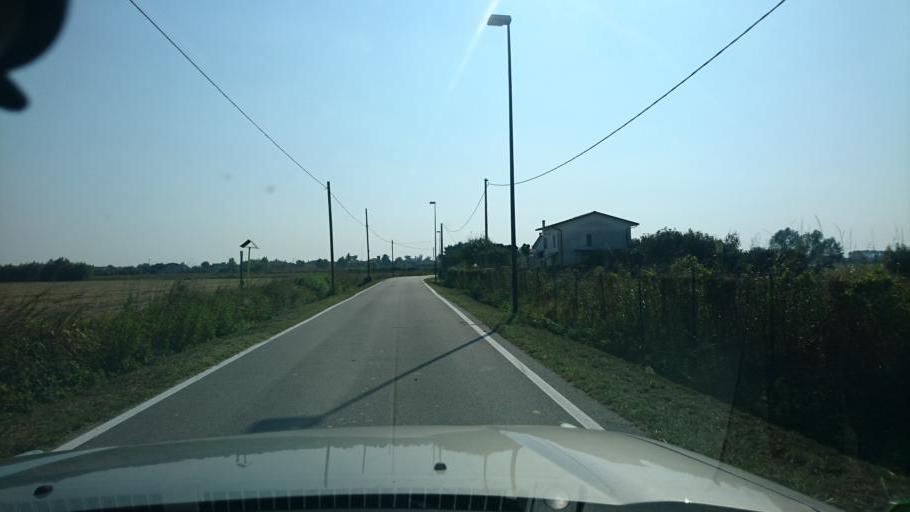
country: IT
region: Veneto
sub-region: Provincia di Vicenza
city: Camisano Vicentino
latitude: 45.5266
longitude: 11.7290
